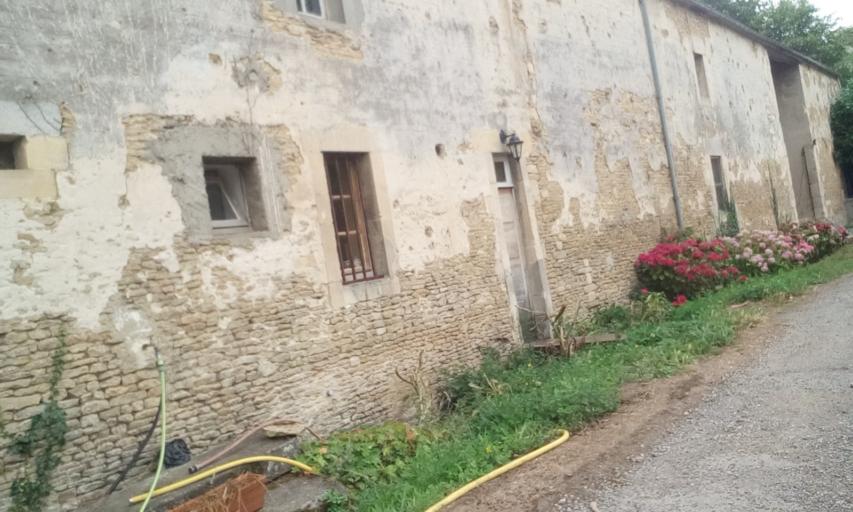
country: FR
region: Lower Normandy
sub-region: Departement du Calvados
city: Bellengreville
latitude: 49.1239
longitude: -0.2031
